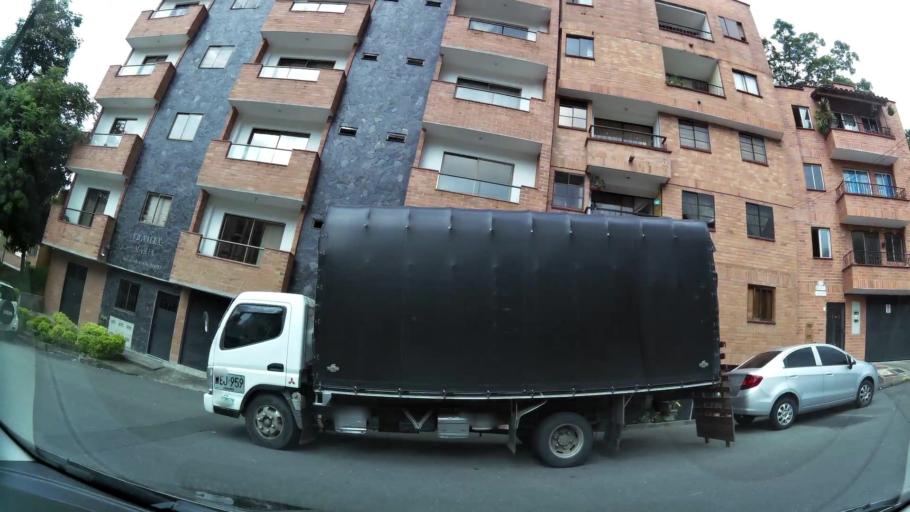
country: CO
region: Antioquia
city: Envigado
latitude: 6.1578
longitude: -75.5958
